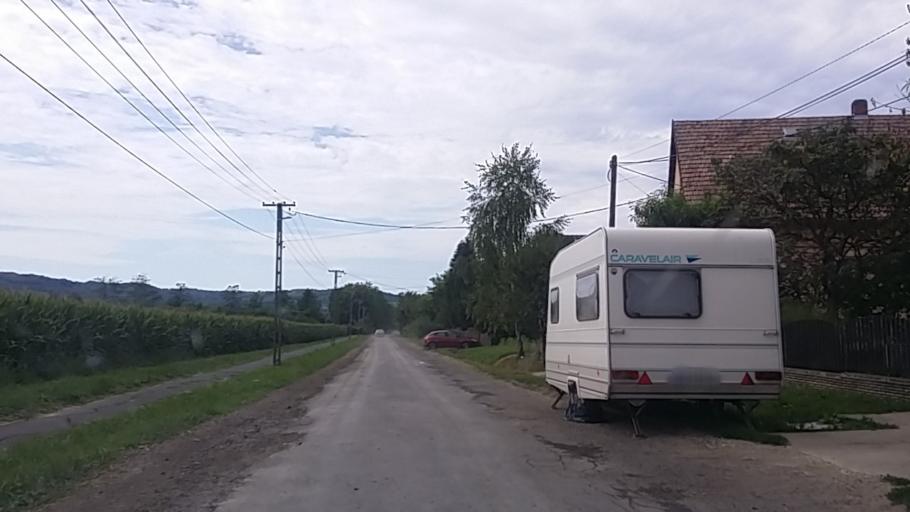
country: HU
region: Somogy
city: Taszar
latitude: 46.3542
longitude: 18.0005
